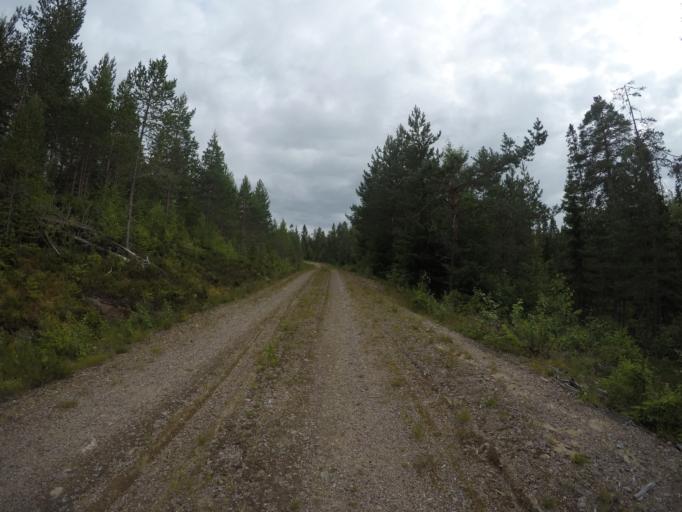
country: SE
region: Vaermland
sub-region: Filipstads Kommun
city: Lesjofors
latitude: 60.2073
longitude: 14.2620
